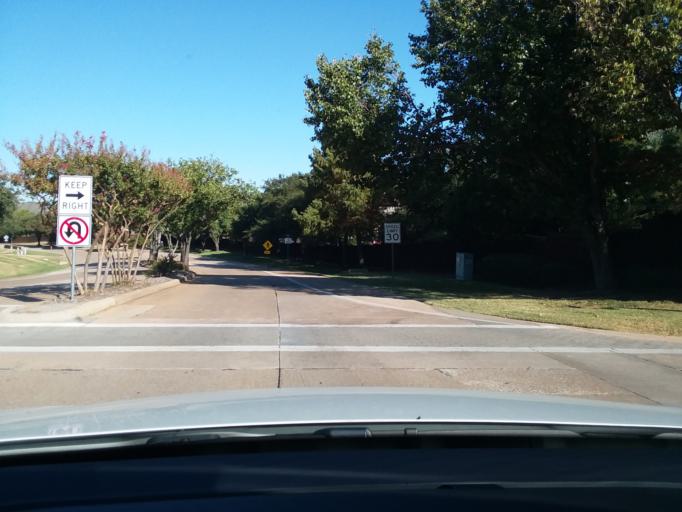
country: US
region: Texas
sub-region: Denton County
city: Highland Village
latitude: 33.0887
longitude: -97.0686
